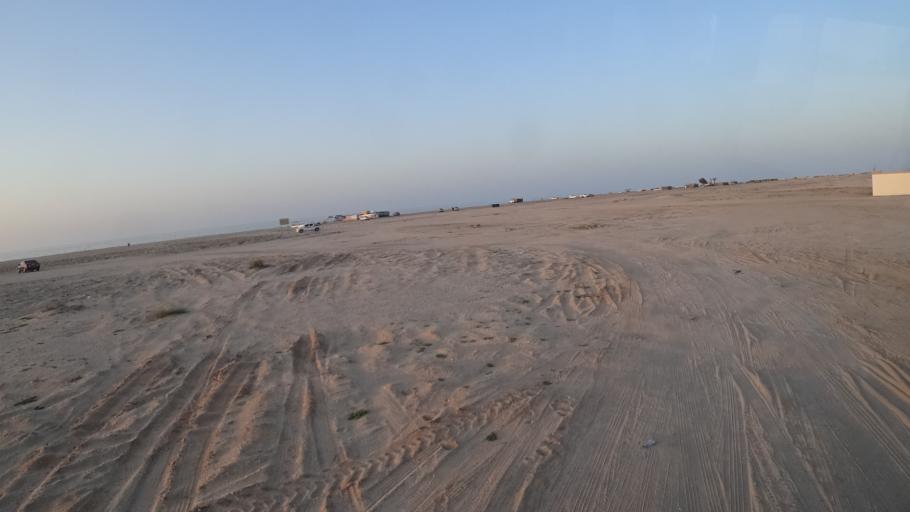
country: OM
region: Ash Sharqiyah
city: Sur
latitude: 22.5309
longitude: 59.7646
